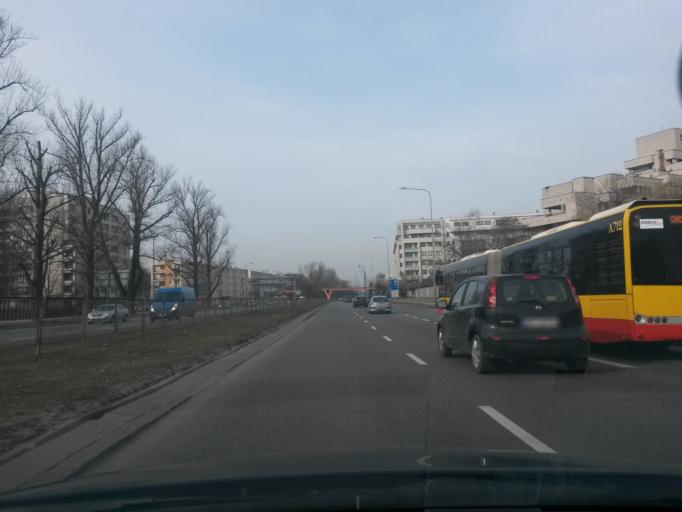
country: PL
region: Masovian Voivodeship
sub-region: Warszawa
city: Mokotow
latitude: 52.1959
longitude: 21.0411
